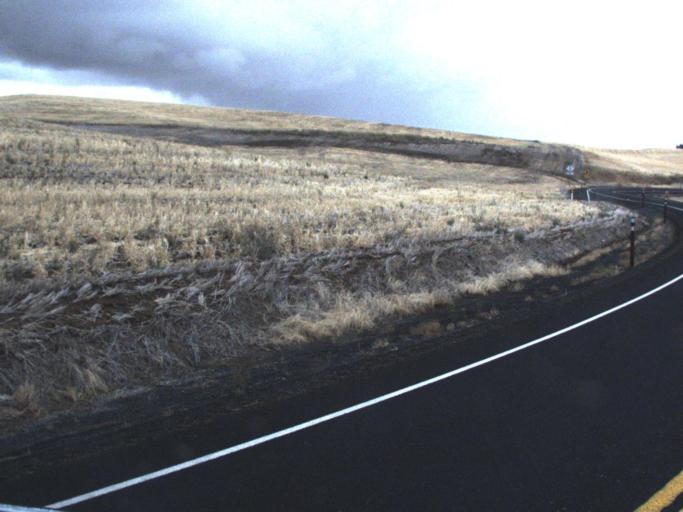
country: US
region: Washington
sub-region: Whitman County
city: Colfax
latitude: 47.1453
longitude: -117.2549
